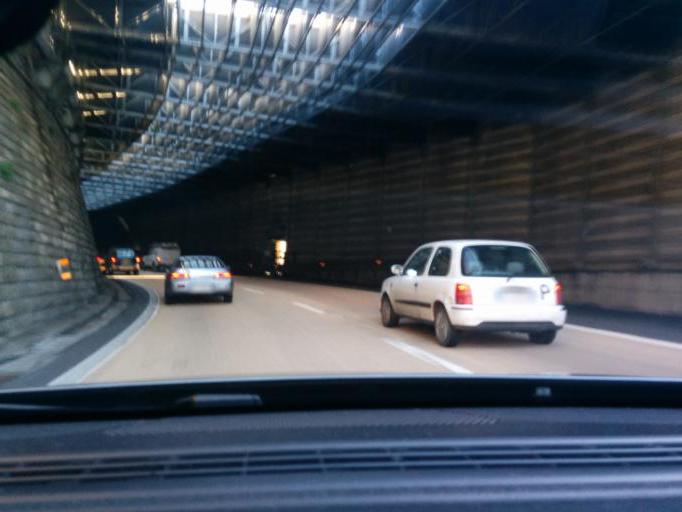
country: IT
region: Liguria
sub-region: Provincia di Genova
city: Genoa
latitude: 44.4298
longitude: 8.8976
